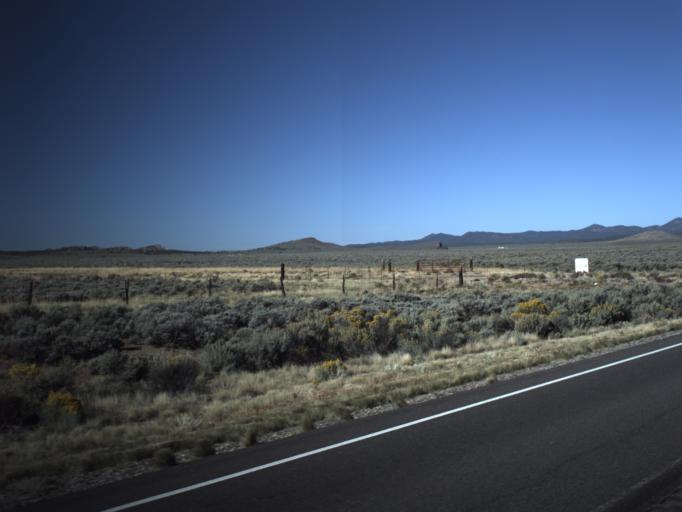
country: US
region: Utah
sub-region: Washington County
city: Enterprise
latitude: 37.7932
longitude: -113.8956
